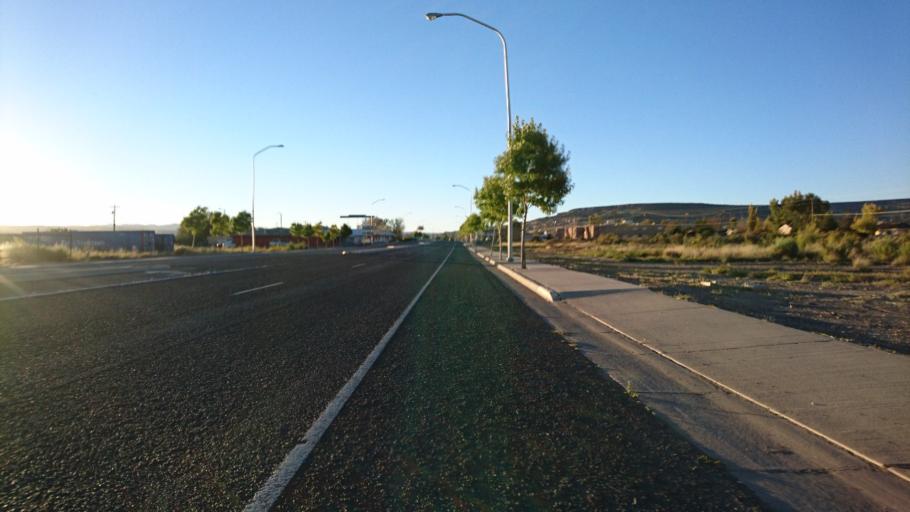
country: US
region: New Mexico
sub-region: Cibola County
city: Grants
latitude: 35.1431
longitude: -107.8350
